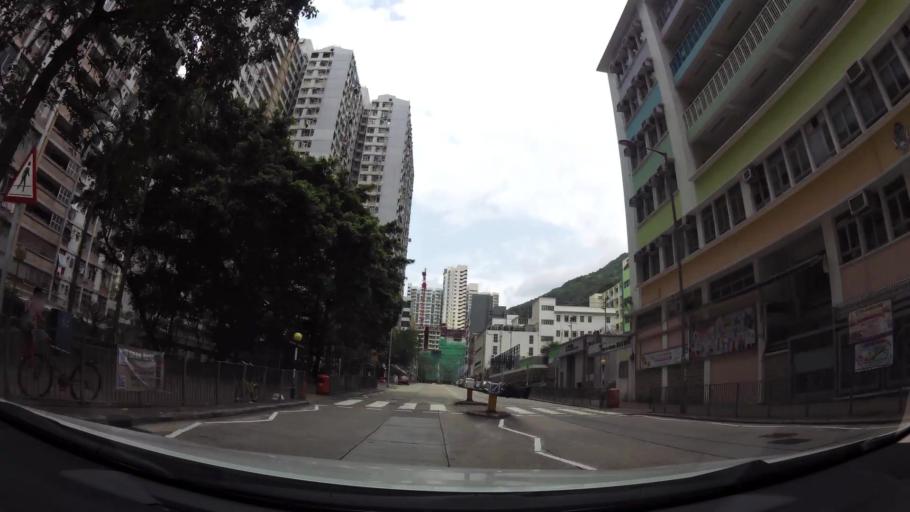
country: HK
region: Sham Shui Po
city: Sham Shui Po
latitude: 22.3395
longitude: 114.1604
